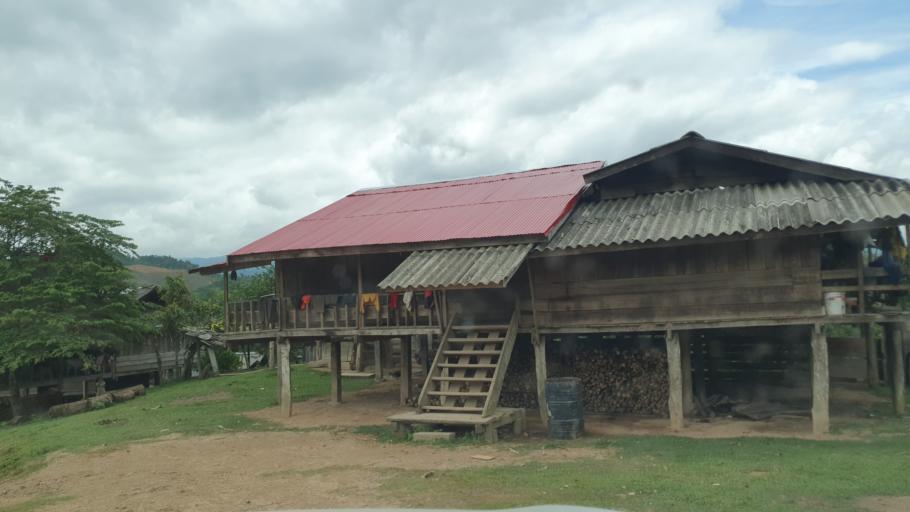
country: VN
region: Nghe An
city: Muong Xen
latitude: 19.3253
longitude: 103.7321
